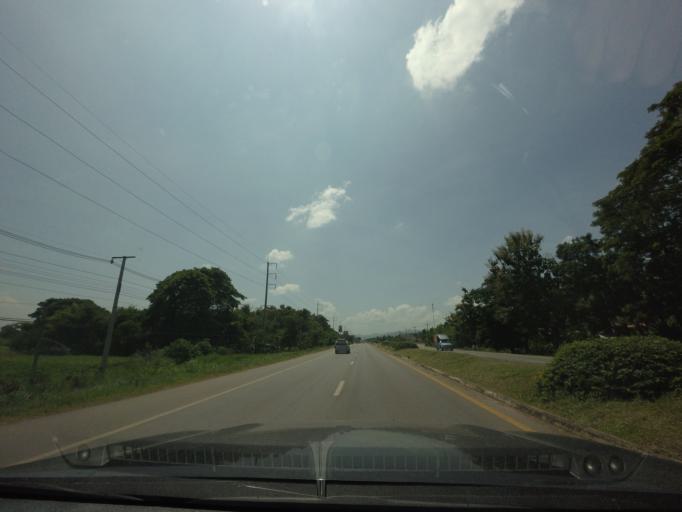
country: TH
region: Phetchabun
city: Lom Sak
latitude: 16.7191
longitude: 101.1828
